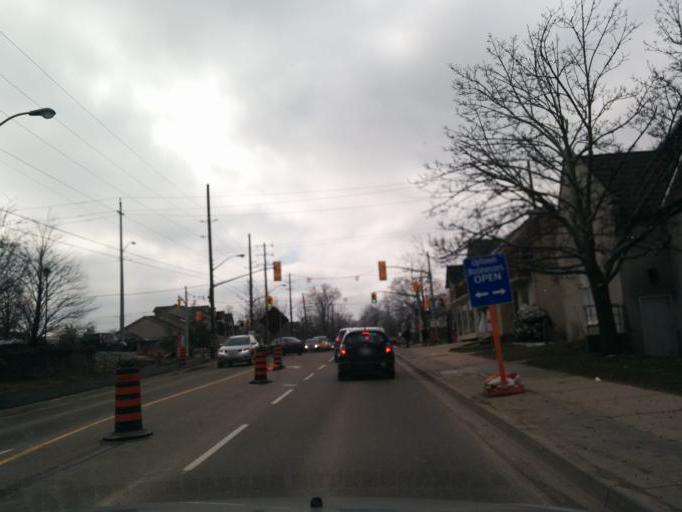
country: CA
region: Ontario
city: Waterloo
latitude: 43.4613
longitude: -80.5218
